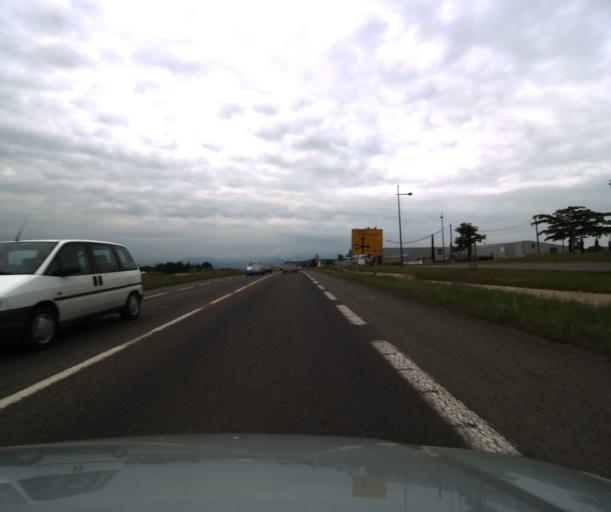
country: FR
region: Midi-Pyrenees
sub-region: Departement des Hautes-Pyrenees
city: Juillan
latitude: 43.1739
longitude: 0.0014
